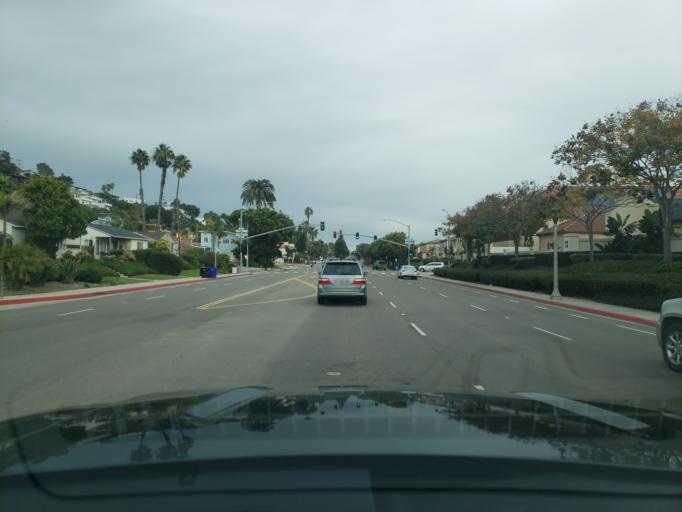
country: US
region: California
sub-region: San Diego County
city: Coronado
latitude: 32.7315
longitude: -117.2233
